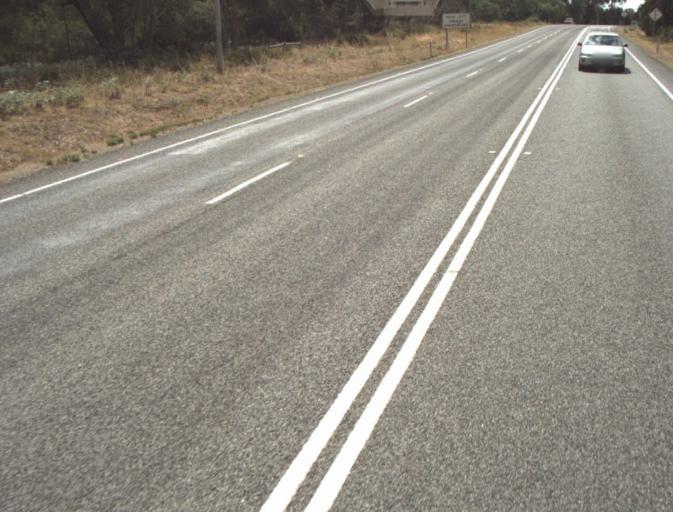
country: AU
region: Tasmania
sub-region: Launceston
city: Mayfield
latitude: -41.2878
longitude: 147.0418
